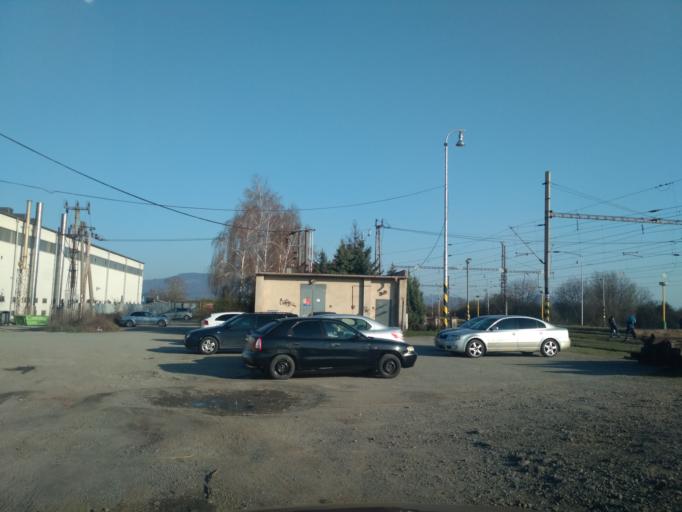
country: SK
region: Kosicky
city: Kosice
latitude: 48.6708
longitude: 21.2951
